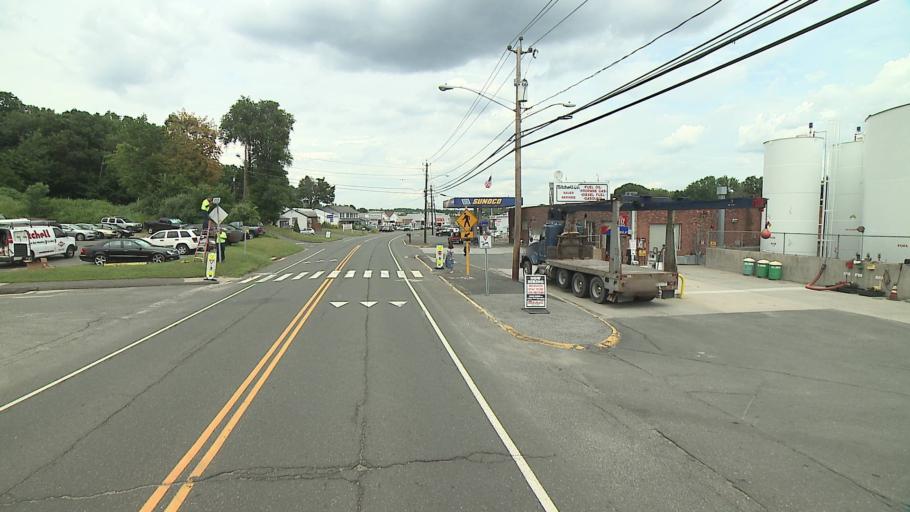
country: US
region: Connecticut
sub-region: Fairfield County
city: Danbury
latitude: 41.4062
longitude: -73.4296
